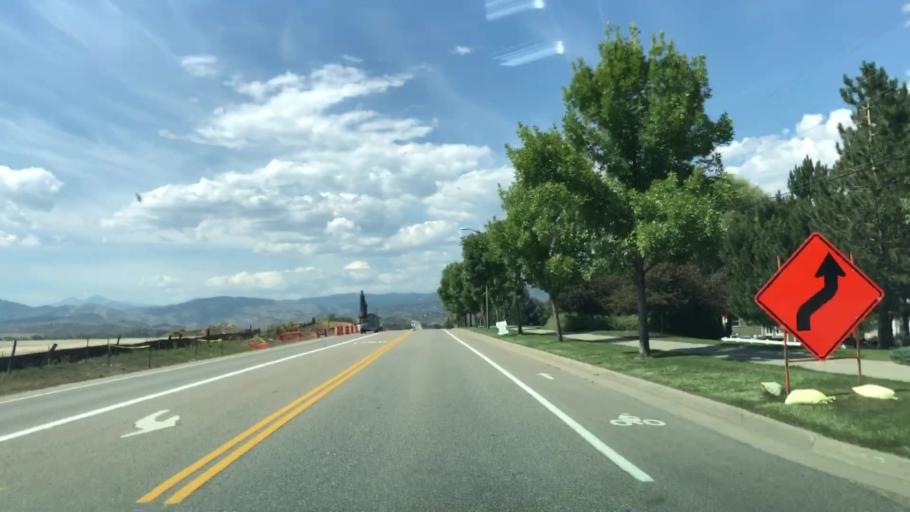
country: US
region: Colorado
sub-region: Larimer County
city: Loveland
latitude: 40.3929
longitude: -105.1366
